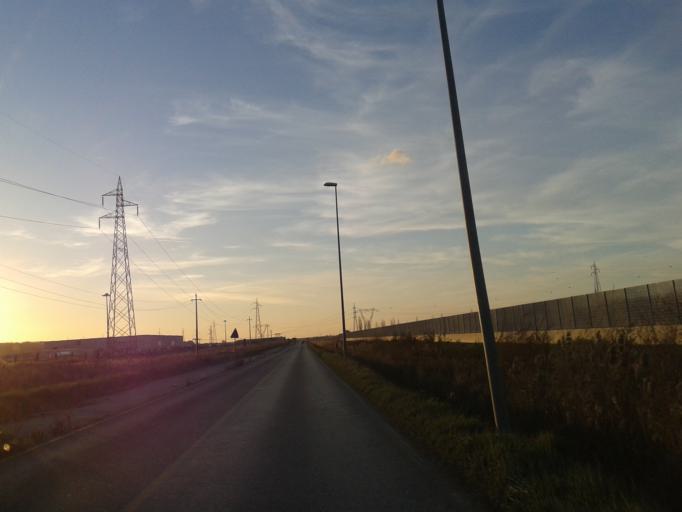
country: IT
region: Tuscany
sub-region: Provincia di Livorno
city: Guasticce
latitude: 43.5971
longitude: 10.3996
